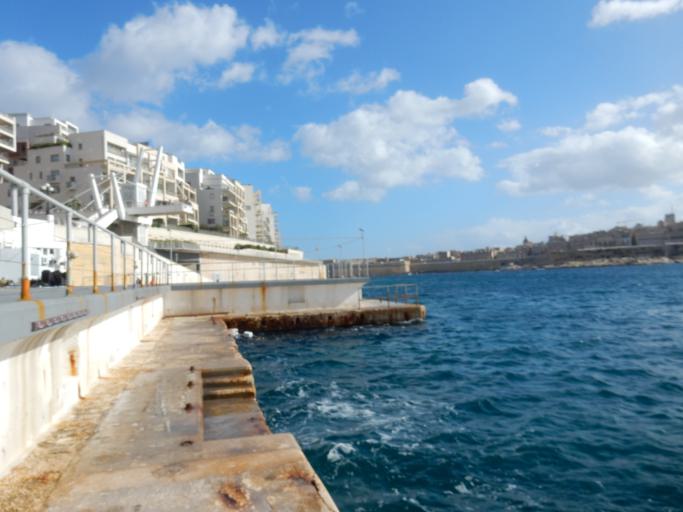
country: MT
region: Il-Belt Valletta
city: Valletta
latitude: 35.9065
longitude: 14.5093
